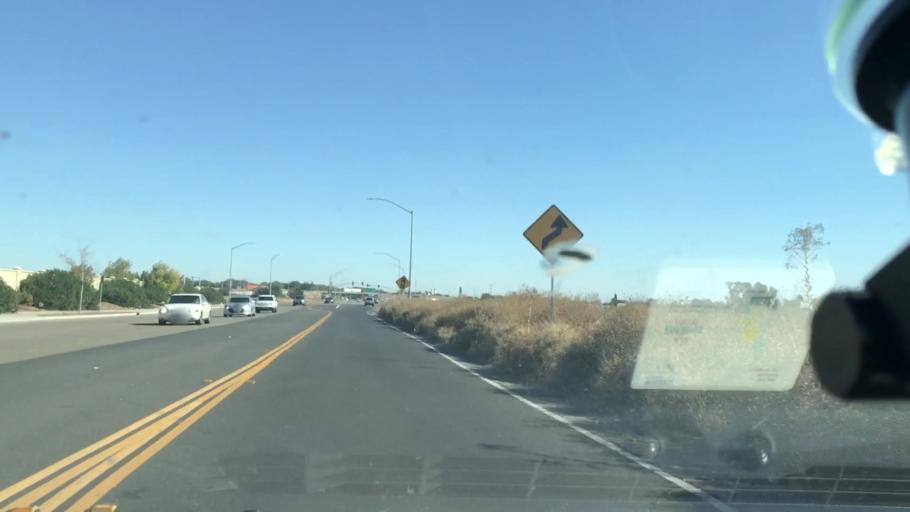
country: US
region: California
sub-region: San Joaquin County
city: Taft Mosswood
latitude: 37.8972
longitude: -121.2932
